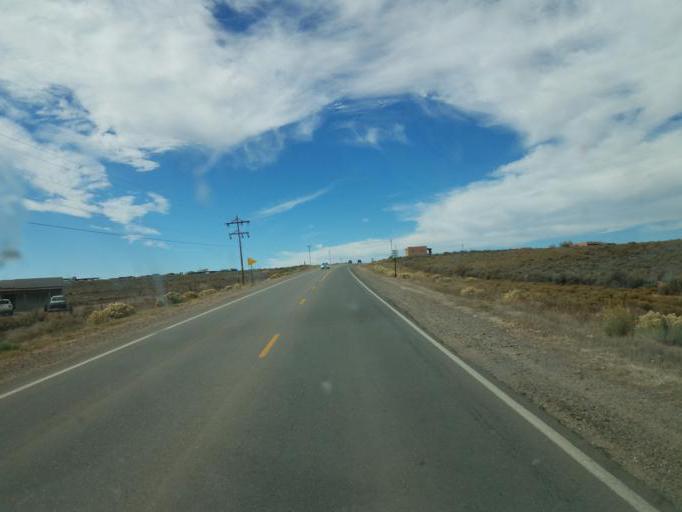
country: US
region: New Mexico
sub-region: Taos County
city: Taos
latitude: 36.4569
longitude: -105.6123
